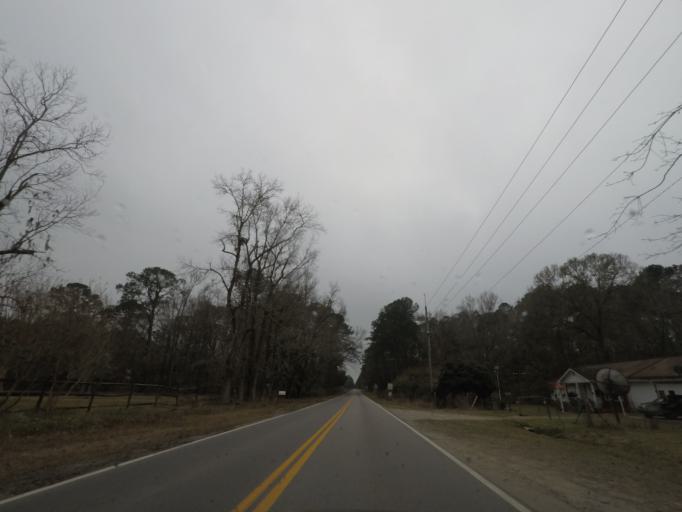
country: US
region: South Carolina
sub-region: Charleston County
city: Ravenel
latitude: 32.7542
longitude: -80.3463
